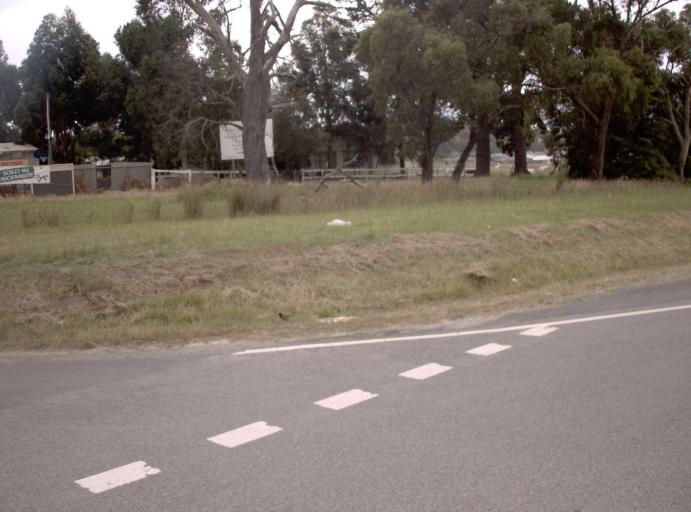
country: AU
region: Victoria
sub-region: Cardinia
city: Officer
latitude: -38.0602
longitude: 145.4487
